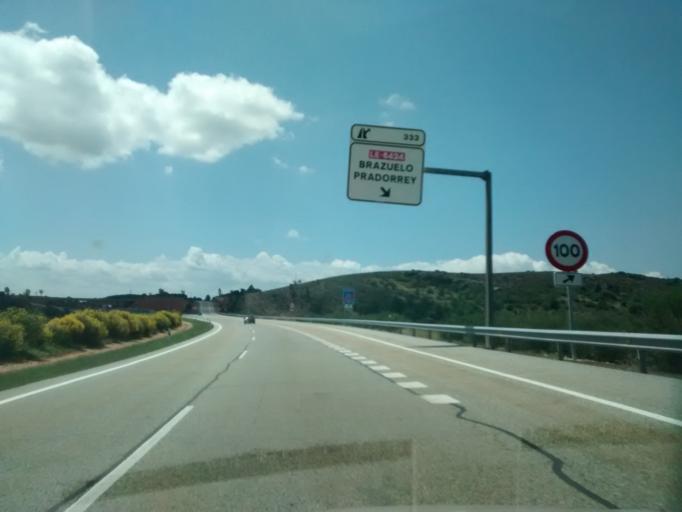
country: ES
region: Castille and Leon
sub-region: Provincia de Leon
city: Brazuelo
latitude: 42.4962
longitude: -6.1271
